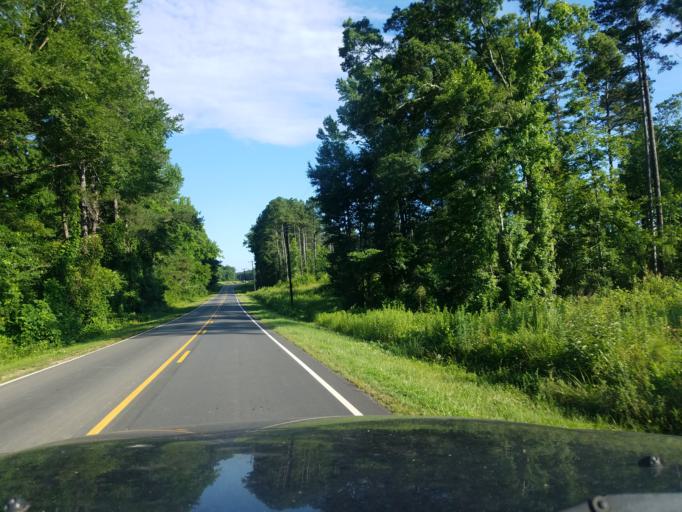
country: US
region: North Carolina
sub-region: Granville County
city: Butner
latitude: 36.1707
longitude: -78.7905
